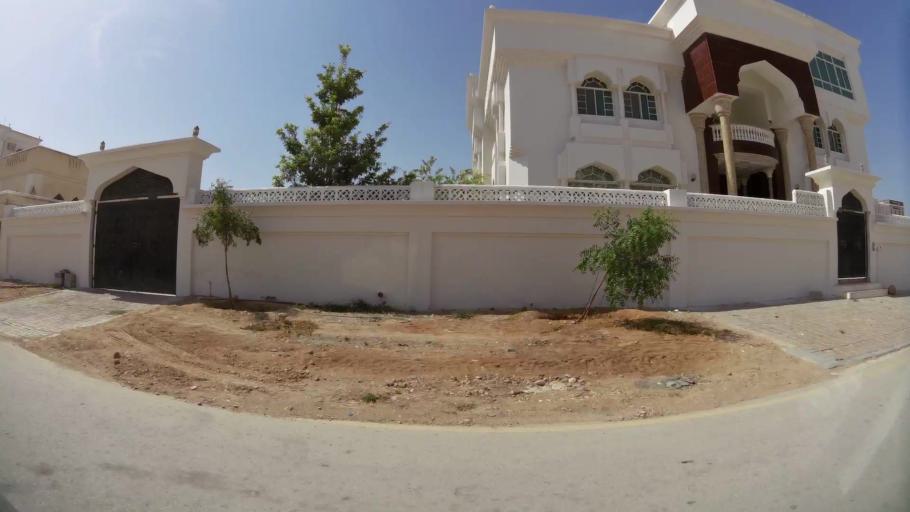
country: OM
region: Zufar
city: Salalah
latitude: 17.0497
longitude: 54.1537
